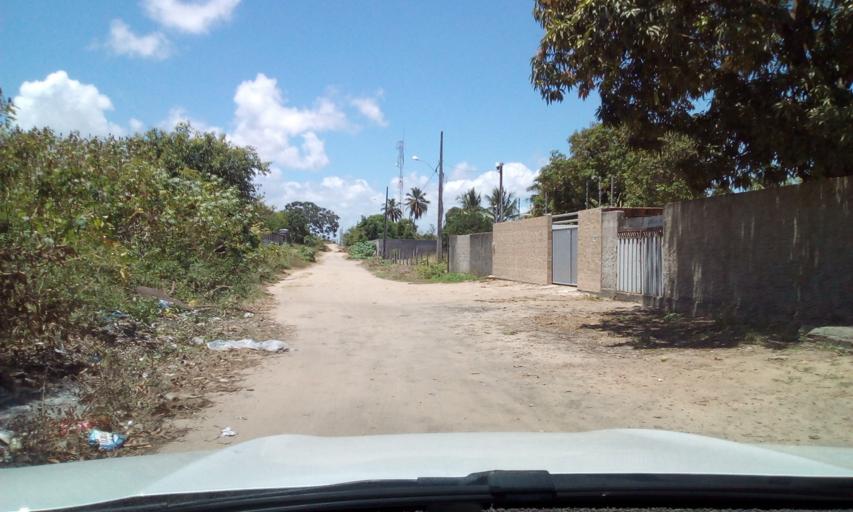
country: BR
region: Paraiba
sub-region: Joao Pessoa
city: Joao Pessoa
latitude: -7.1517
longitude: -34.8069
